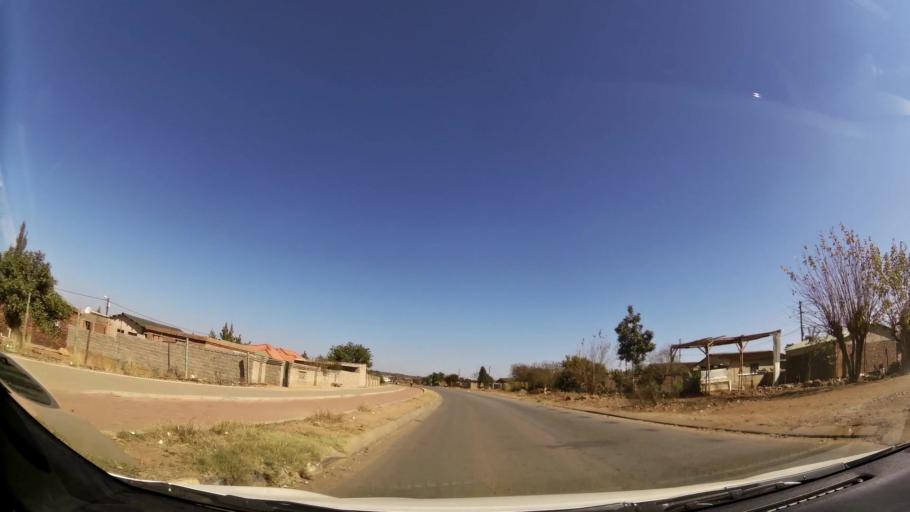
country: ZA
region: Limpopo
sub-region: Capricorn District Municipality
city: Polokwane
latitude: -23.8950
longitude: 29.4150
